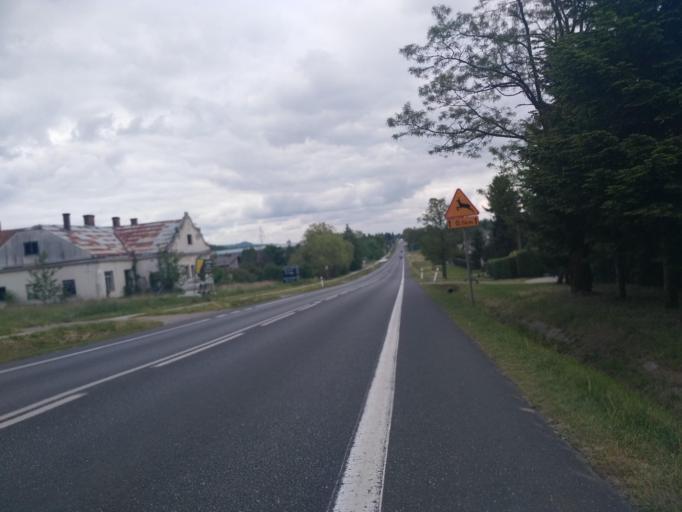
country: PL
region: Subcarpathian Voivodeship
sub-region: Powiat krosnienski
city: Jedlicze
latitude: 49.7225
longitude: 21.6937
